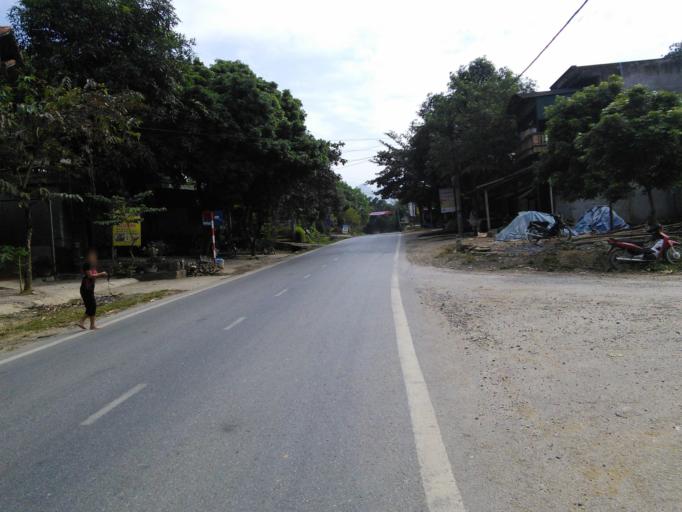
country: VN
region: Lao Cai
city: Lao Cai
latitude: 22.4634
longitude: 103.9474
